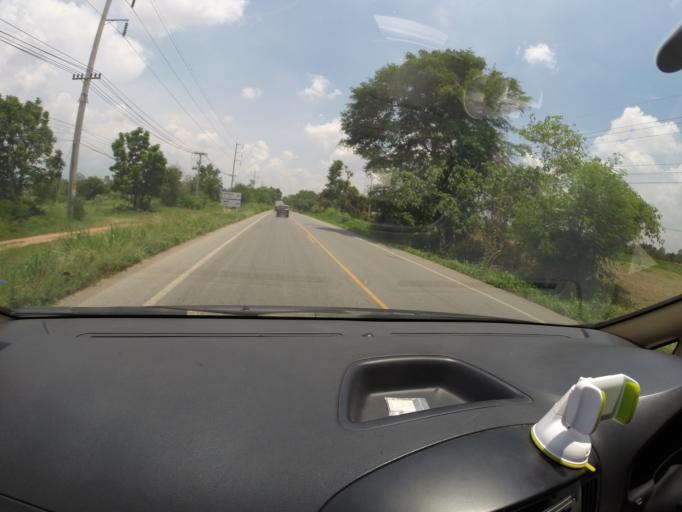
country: TH
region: Nakhon Ratchasima
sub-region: Amphoe Thepharak
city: Thepharak
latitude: 15.1265
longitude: 101.5477
